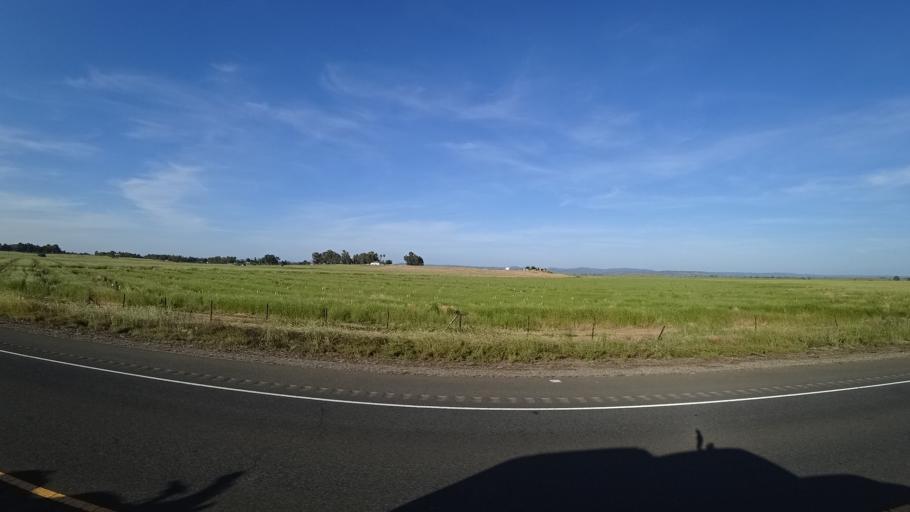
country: US
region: California
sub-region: Placer County
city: Sheridan
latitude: 38.9688
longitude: -121.3663
